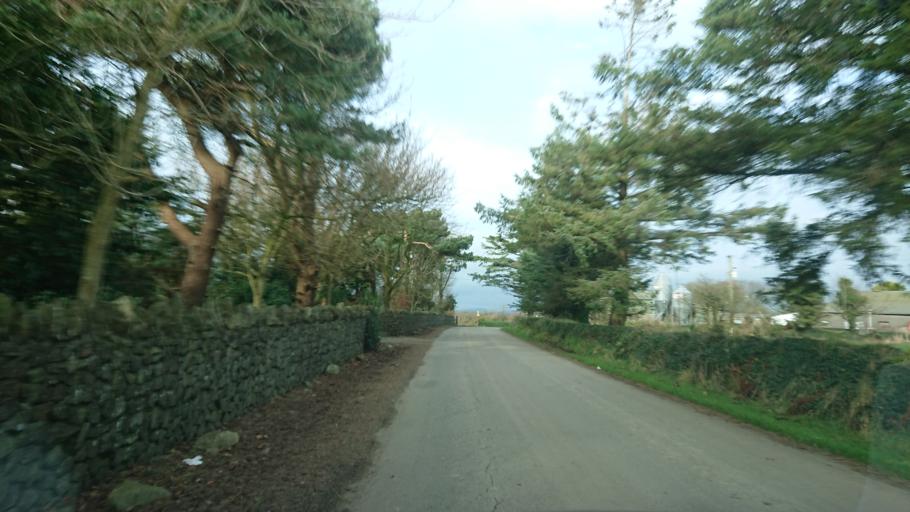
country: IE
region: Munster
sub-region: Waterford
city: Tra Mhor
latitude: 52.1493
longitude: -7.2117
